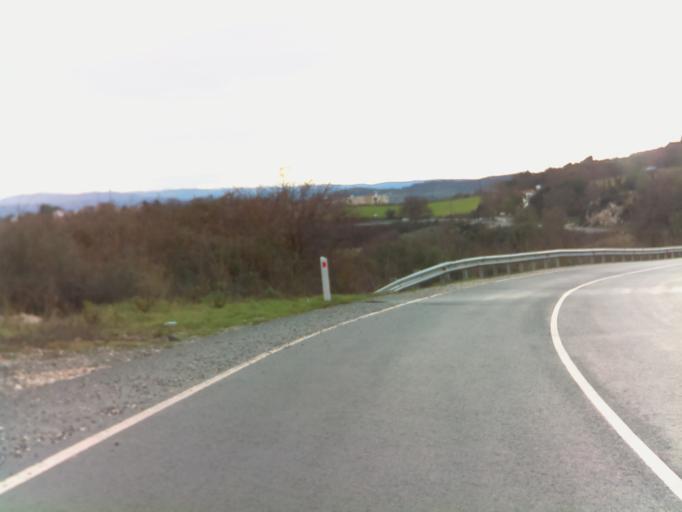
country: CY
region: Pafos
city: Tala
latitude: 34.8951
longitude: 32.4667
